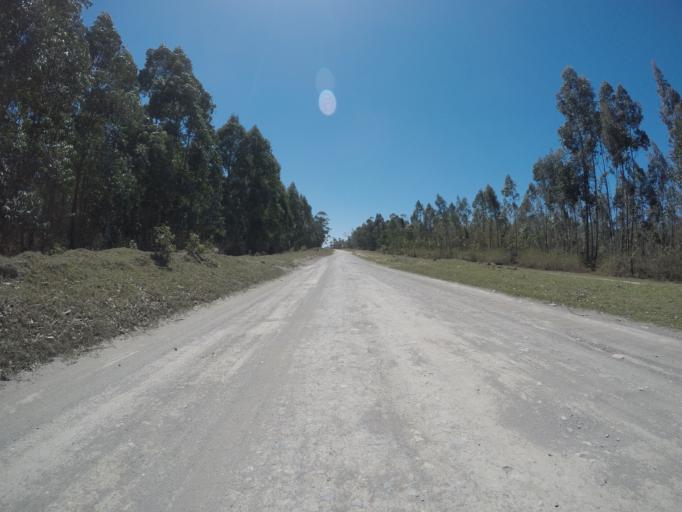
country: ZA
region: Eastern Cape
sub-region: OR Tambo District Municipality
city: Libode
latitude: -31.9516
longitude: 29.0239
